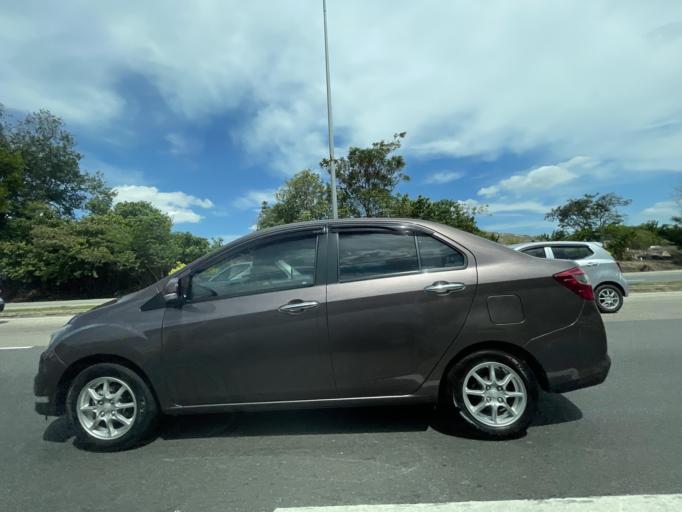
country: MY
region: Melaka
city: Batu Berendam
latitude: 2.2403
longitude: 102.2241
